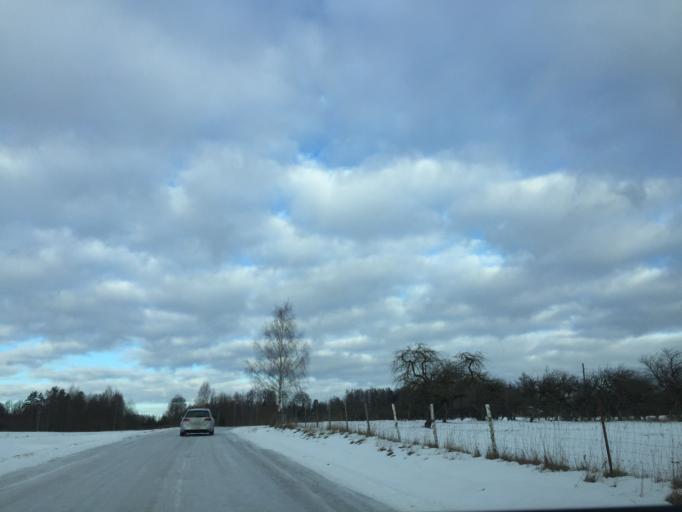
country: LV
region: Lielvarde
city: Lielvarde
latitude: 56.5677
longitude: 24.7336
